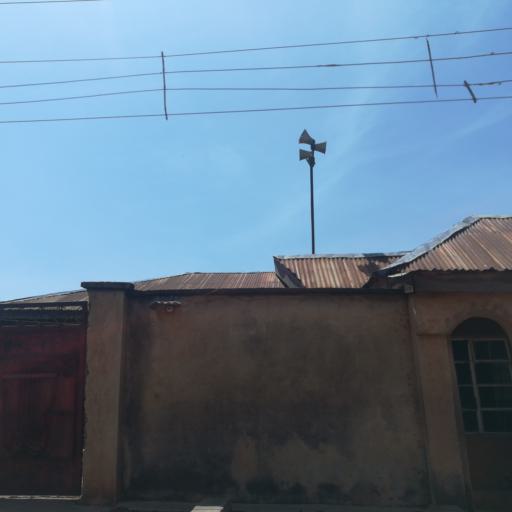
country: NG
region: Plateau
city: Bukuru
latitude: 9.7975
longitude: 8.8648
